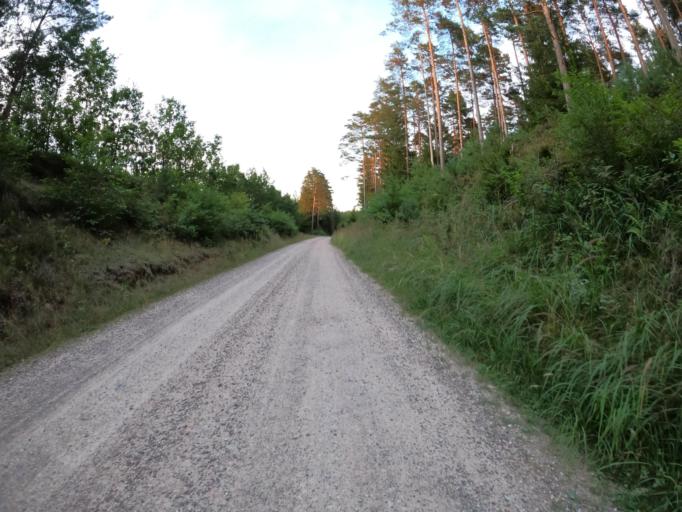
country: PL
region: West Pomeranian Voivodeship
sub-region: Powiat koszalinski
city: Sianow
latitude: 54.1014
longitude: 16.4034
